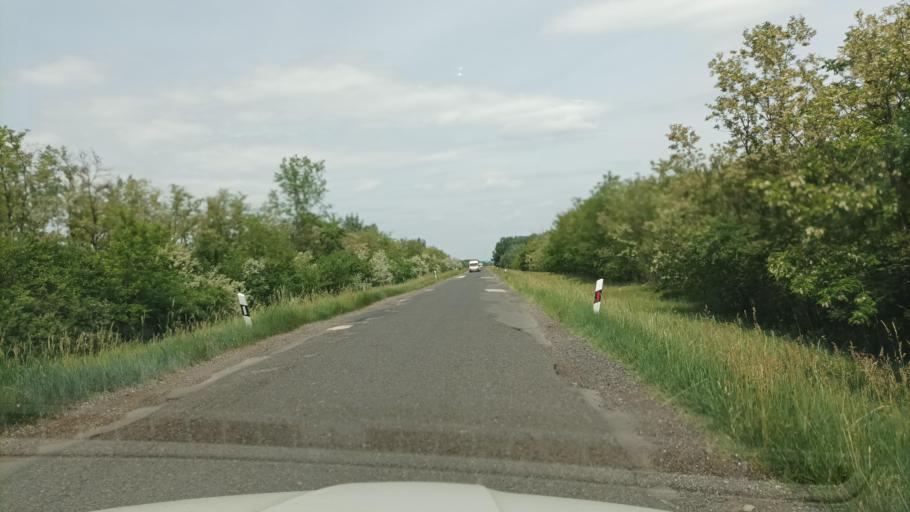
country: HU
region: Pest
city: Szigetujfalu
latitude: 47.2572
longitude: 18.9296
